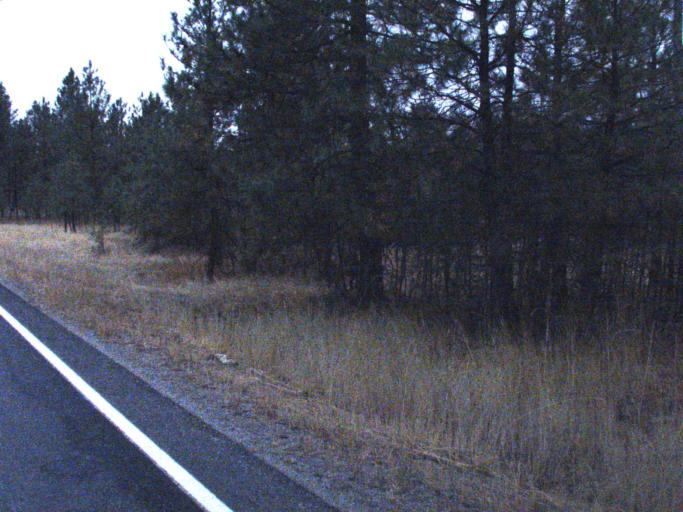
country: US
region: Washington
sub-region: Spokane County
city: Fairchild Air Force Base
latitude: 47.8596
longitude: -117.8452
